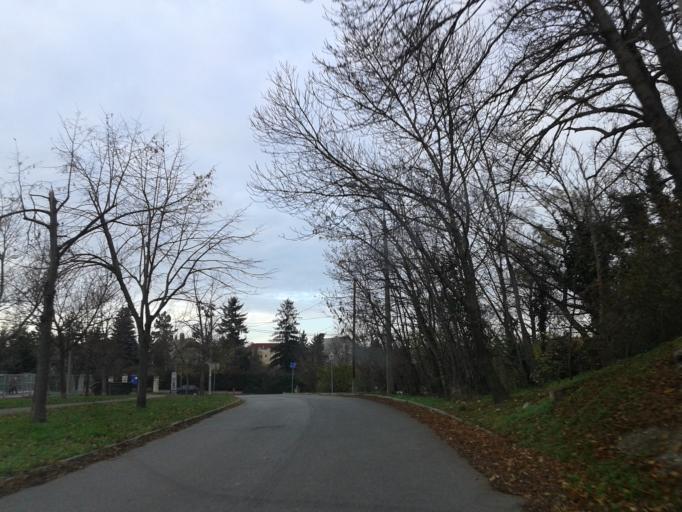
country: HU
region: Budapest
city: Budapest XXII. keruelet
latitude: 47.4082
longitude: 19.0102
